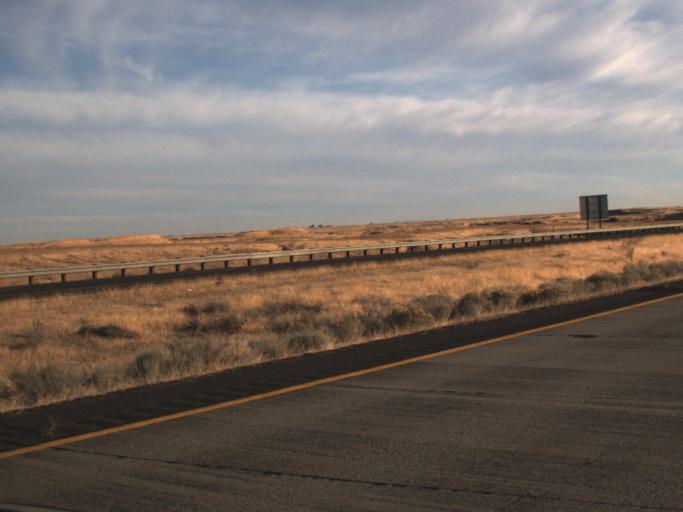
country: US
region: Washington
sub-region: Franklin County
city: Connell
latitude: 46.5775
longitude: -118.9785
